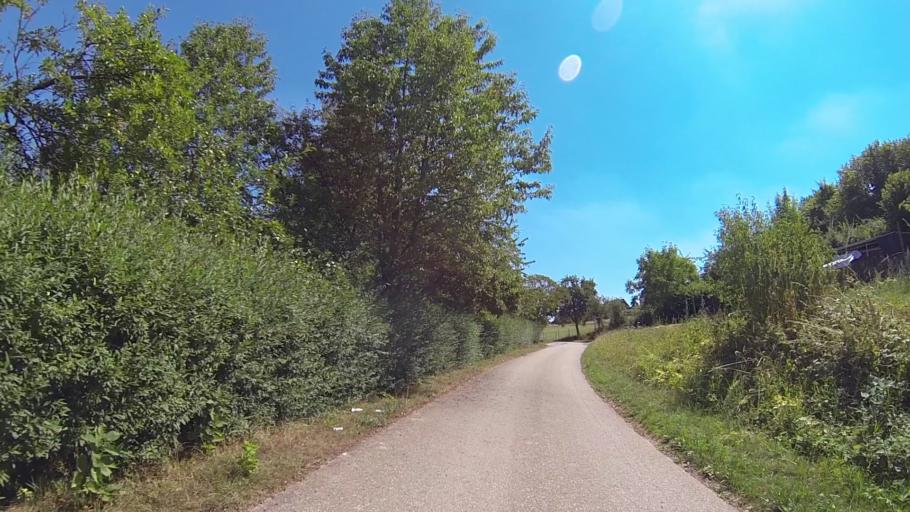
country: LU
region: Grevenmacher
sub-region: Canton de Grevenmacher
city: Wormeldange
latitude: 49.6063
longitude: 6.4183
